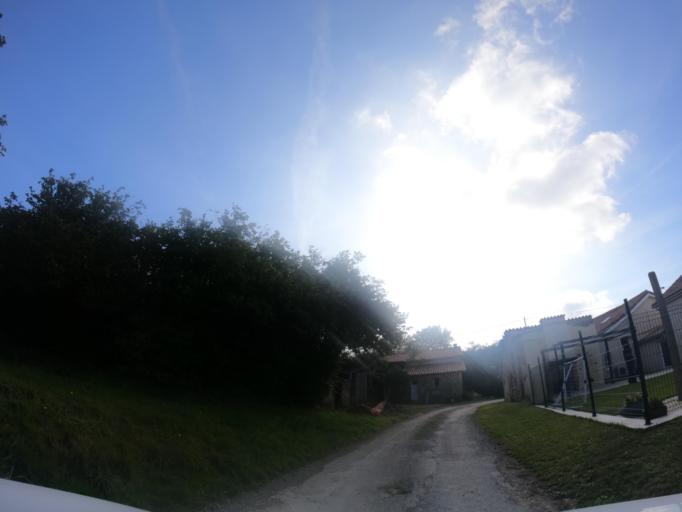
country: FR
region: Poitou-Charentes
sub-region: Departement des Deux-Sevres
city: Courlay
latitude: 46.7878
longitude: -0.5977
